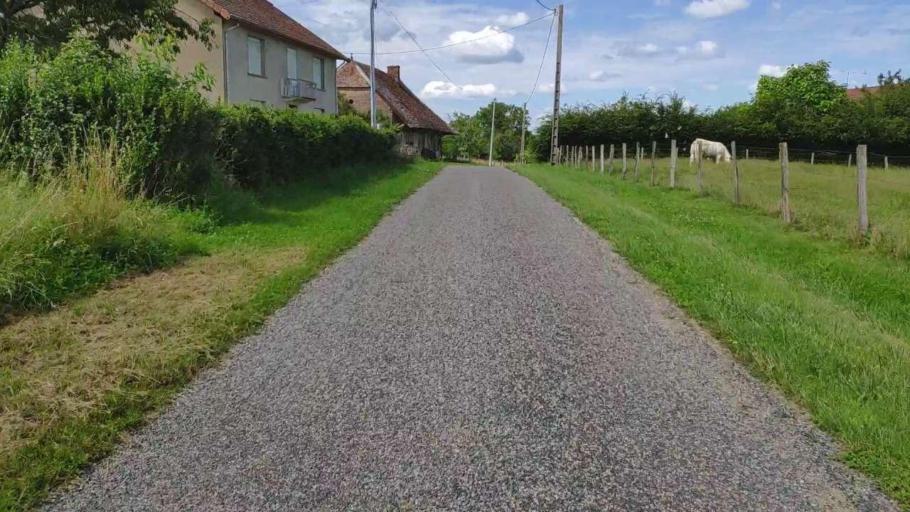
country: FR
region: Franche-Comte
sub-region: Departement du Jura
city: Bletterans
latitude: 46.8226
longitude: 5.4512
